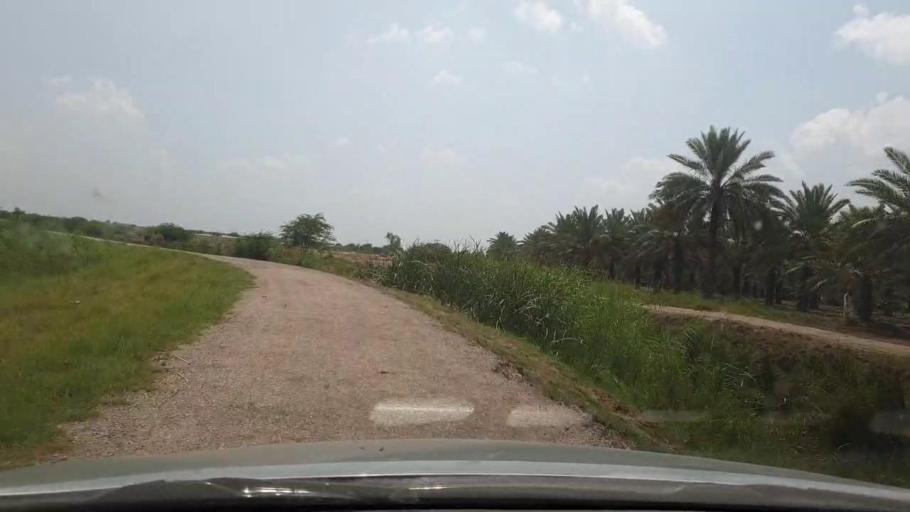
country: PK
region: Sindh
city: Kot Diji
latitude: 27.3925
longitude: 68.7186
